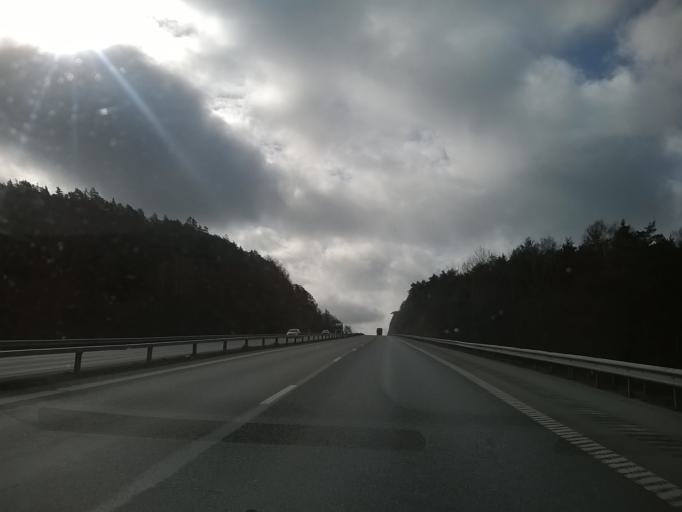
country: SE
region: Halland
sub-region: Kungsbacka Kommun
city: Frillesas
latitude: 57.3154
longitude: 12.2103
